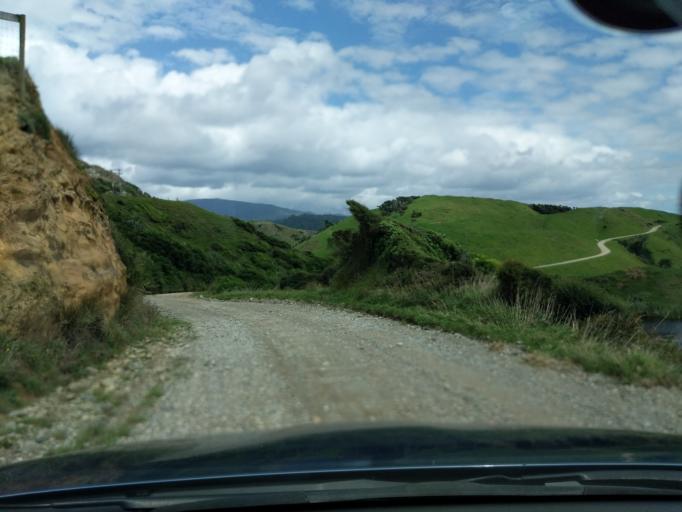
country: NZ
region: Tasman
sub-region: Tasman District
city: Takaka
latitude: -40.6695
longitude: 172.3994
